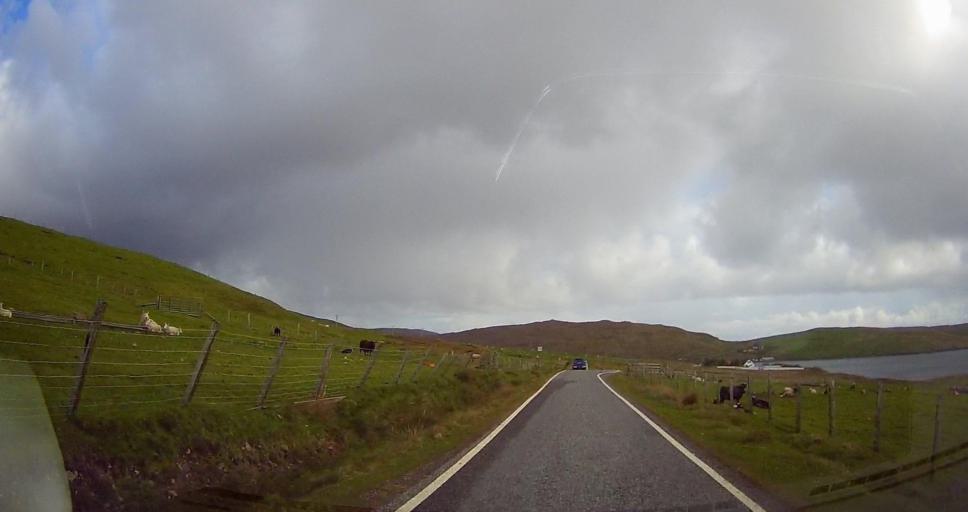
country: GB
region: Scotland
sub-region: Shetland Islands
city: Lerwick
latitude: 60.5323
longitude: -1.3622
